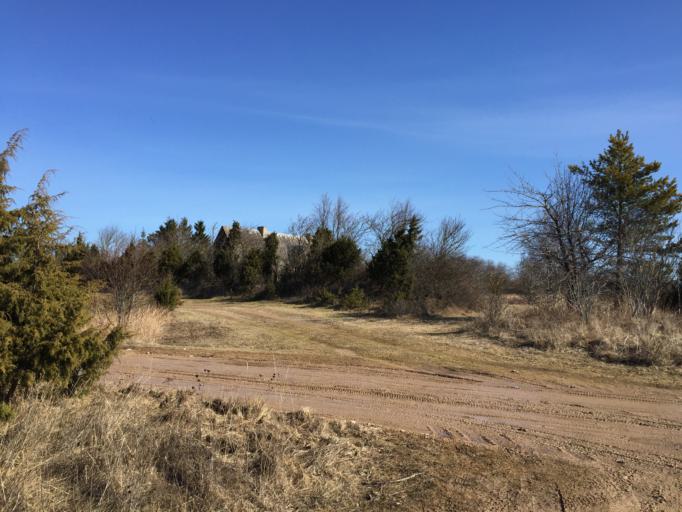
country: EE
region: Laeaene
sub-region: Haapsalu linn
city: Haapsalu
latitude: 58.6460
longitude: 23.5135
